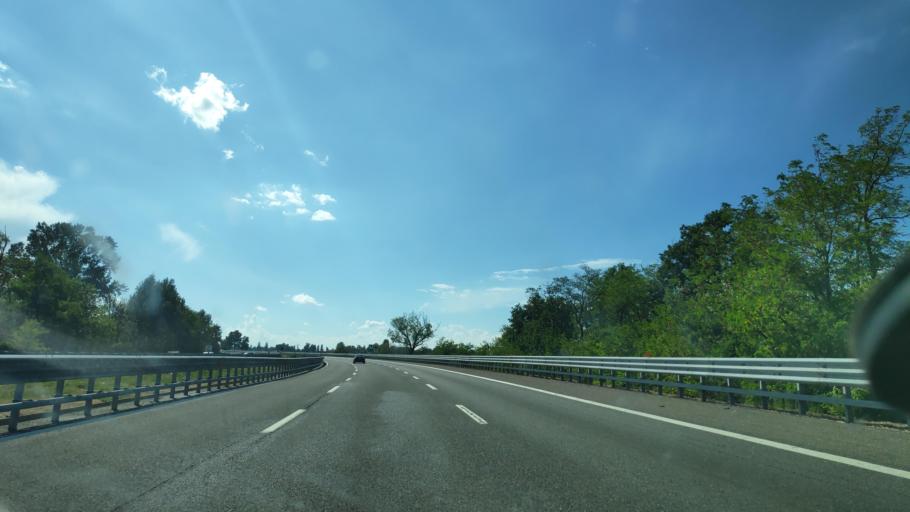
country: IT
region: Piedmont
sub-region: Provincia di Alessandria
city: Castelnuovo Scrivia
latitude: 44.9520
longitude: 8.8668
